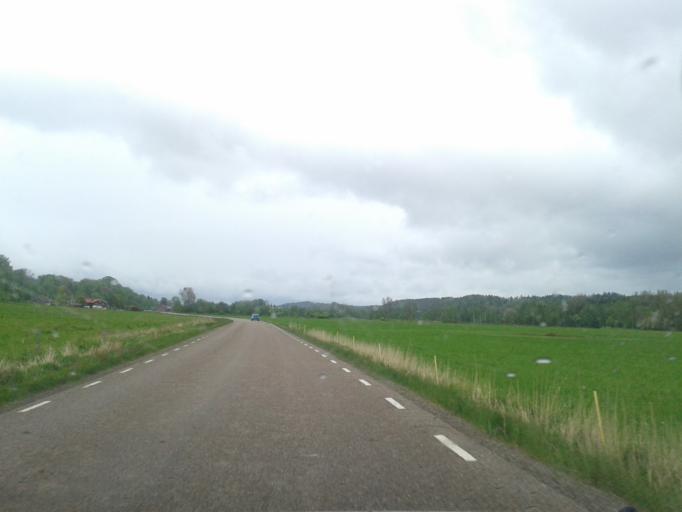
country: SE
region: Vaestra Goetaland
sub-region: Lilla Edets Kommun
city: Lodose
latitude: 58.0258
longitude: 12.1379
